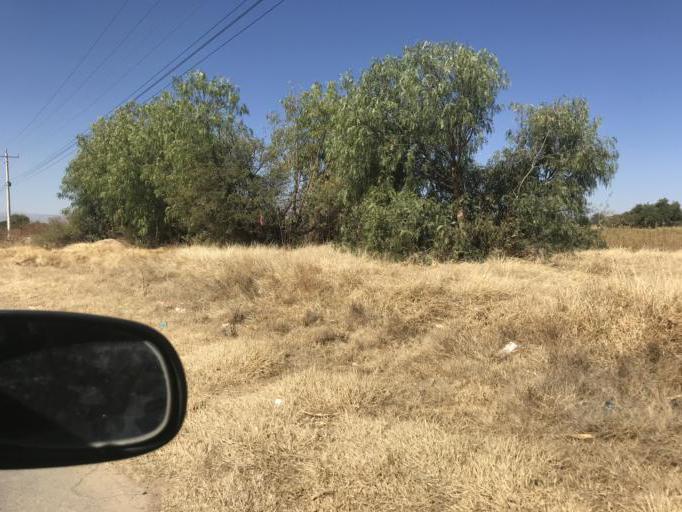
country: BO
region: Cochabamba
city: Cliza
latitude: -17.6013
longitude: -65.9726
